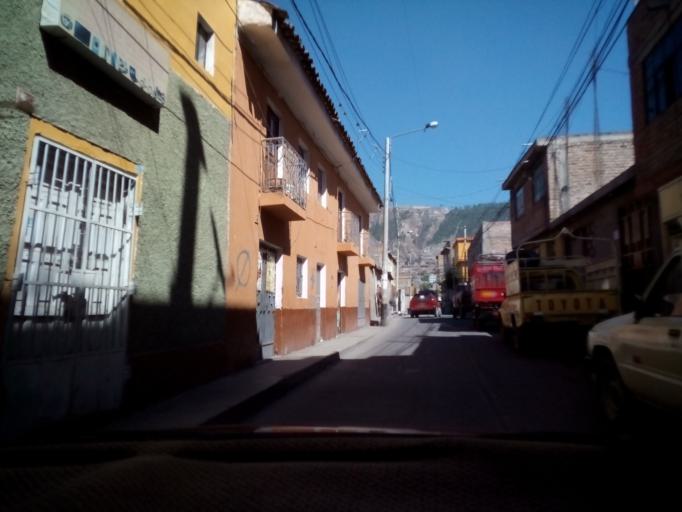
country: PE
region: Ayacucho
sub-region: Provincia de Huamanga
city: Ayacucho
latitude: -13.1575
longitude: -74.2214
